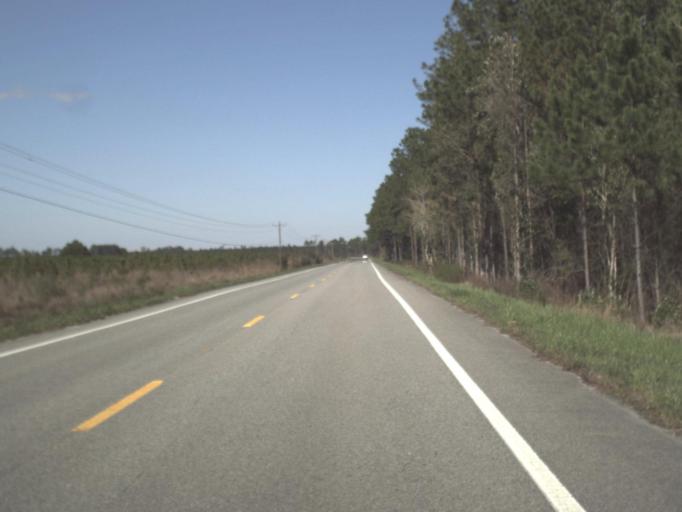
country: US
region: Florida
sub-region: Gulf County
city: Wewahitchka
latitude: 29.9684
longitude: -85.1712
